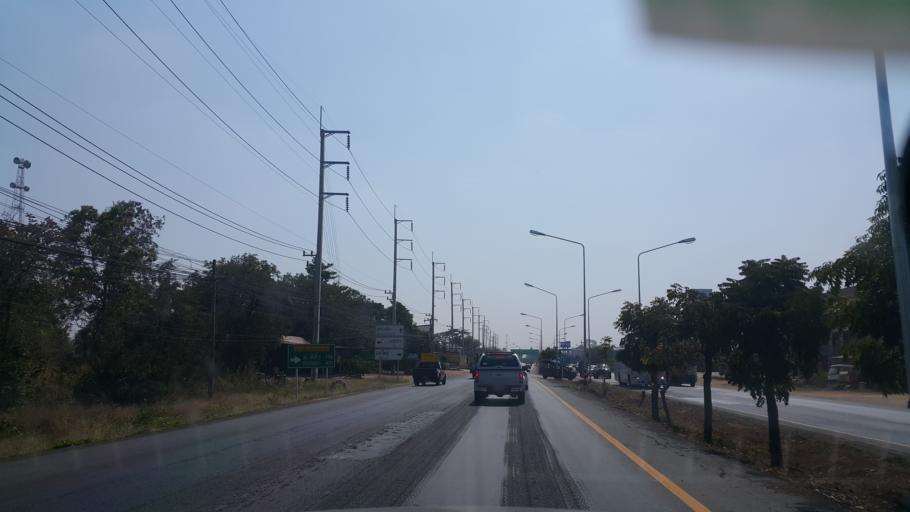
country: TH
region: Nakhon Ratchasima
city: Sida
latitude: 15.5522
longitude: 102.5493
